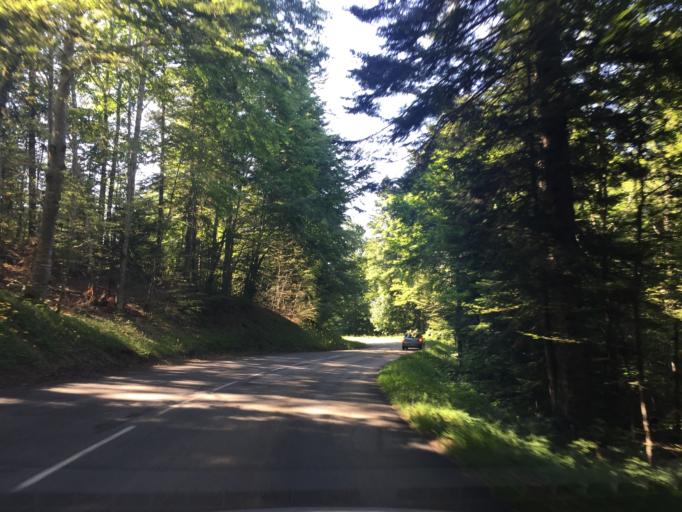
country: FR
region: Rhone-Alpes
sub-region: Departement de la Drome
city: Saint-Jean-en-Royans
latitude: 44.9329
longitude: 5.3173
